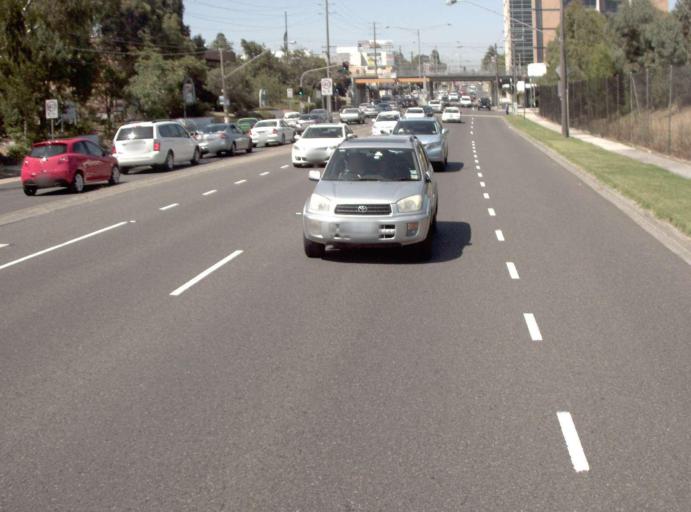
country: AU
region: Victoria
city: Ashburton
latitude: -37.8728
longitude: 145.0920
